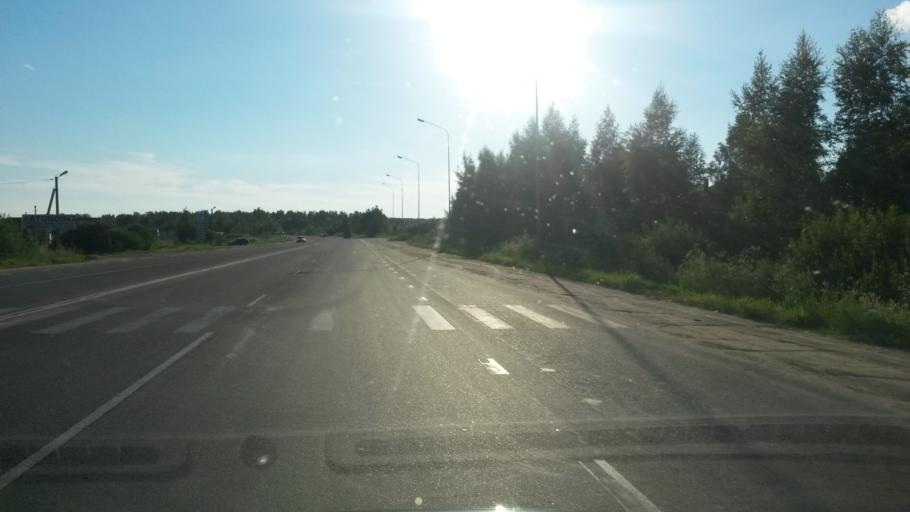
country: RU
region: Ivanovo
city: Novo-Talitsy
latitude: 57.0213
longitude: 40.8997
